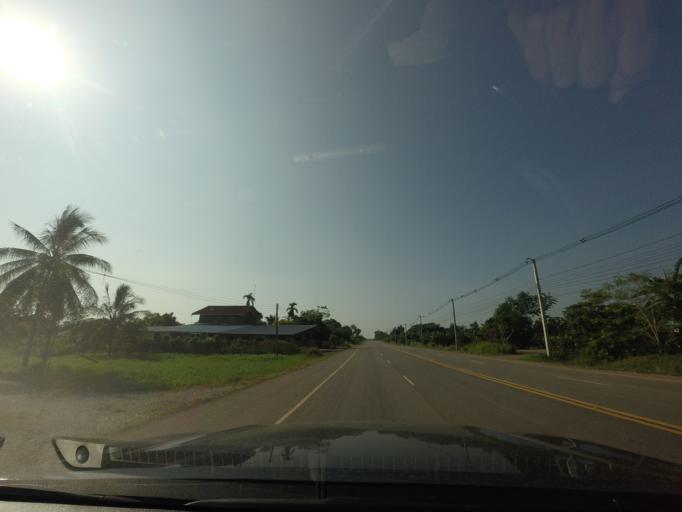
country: TH
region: Phetchabun
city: Lom Kao
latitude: 16.8288
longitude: 101.1808
